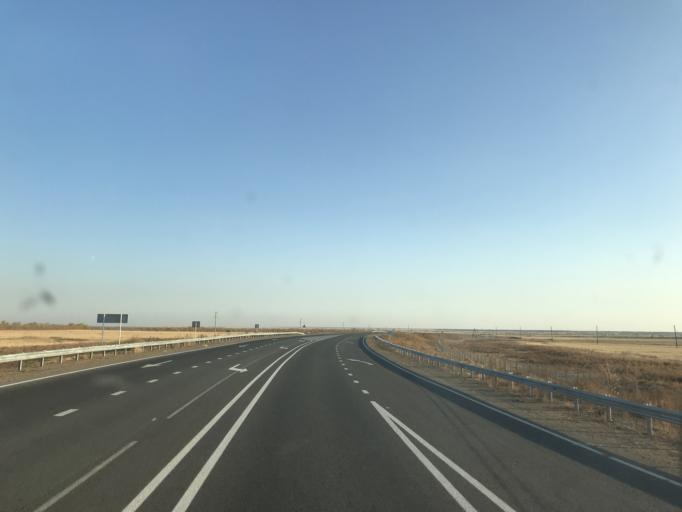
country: KZ
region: Pavlodar
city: Kurchatov
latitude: 51.0494
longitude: 79.1221
